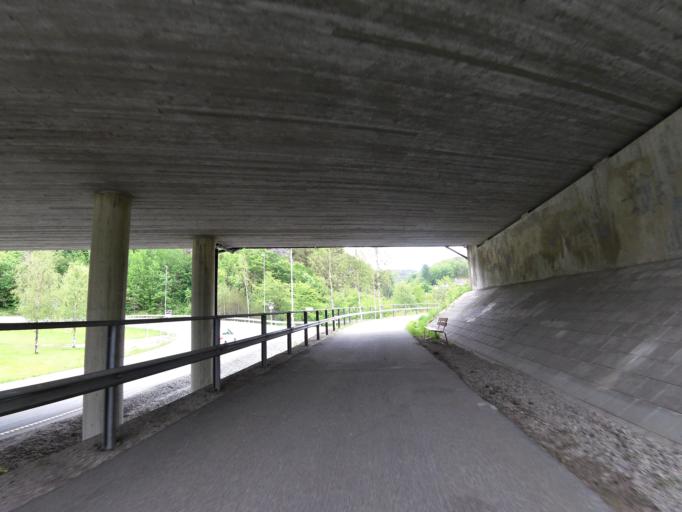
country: NO
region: Vest-Agder
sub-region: Flekkefjord
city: Flekkefjord
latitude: 58.2980
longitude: 6.6795
